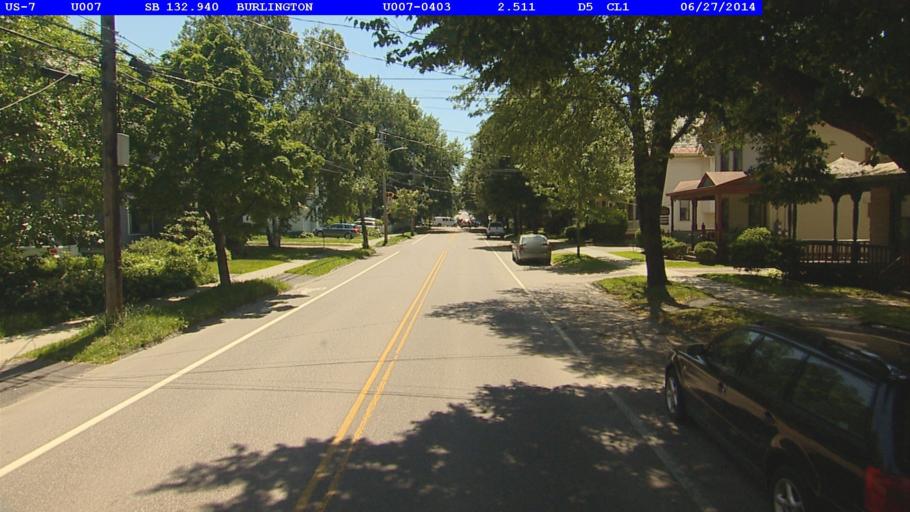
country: US
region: Vermont
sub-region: Chittenden County
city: Burlington
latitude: 44.4817
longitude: -73.2058
